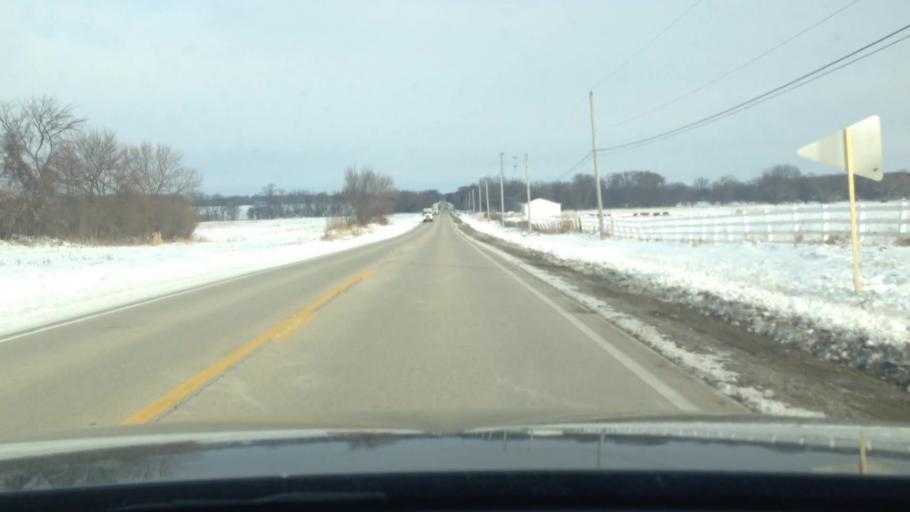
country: US
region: Illinois
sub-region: McHenry County
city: Woodstock
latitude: 42.3649
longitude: -88.4431
